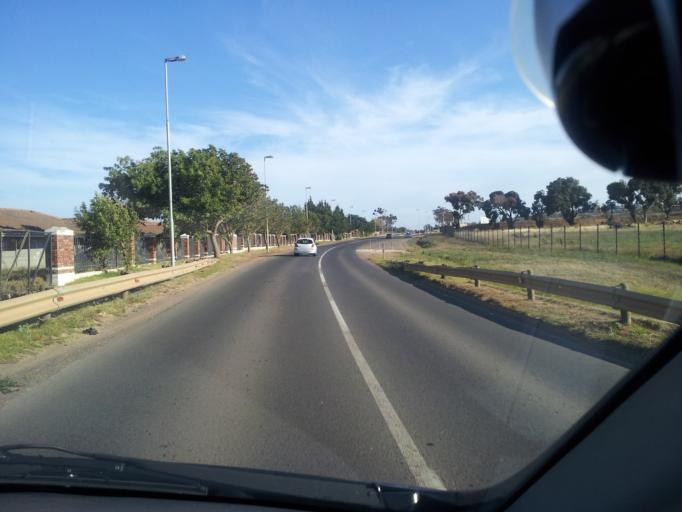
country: ZA
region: Western Cape
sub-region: City of Cape Town
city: Kraaifontein
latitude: -33.8158
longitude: 18.6336
